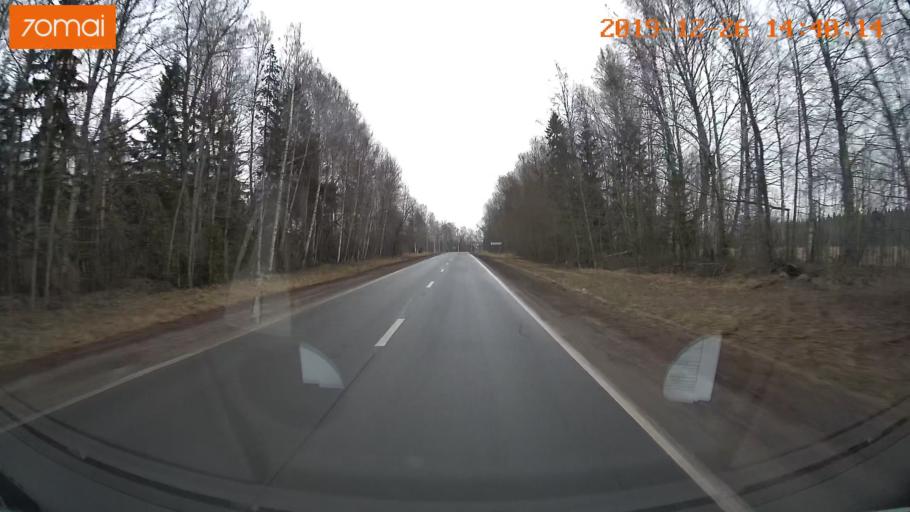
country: RU
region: Jaroslavl
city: Poshekhon'ye
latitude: 58.3772
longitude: 38.9950
